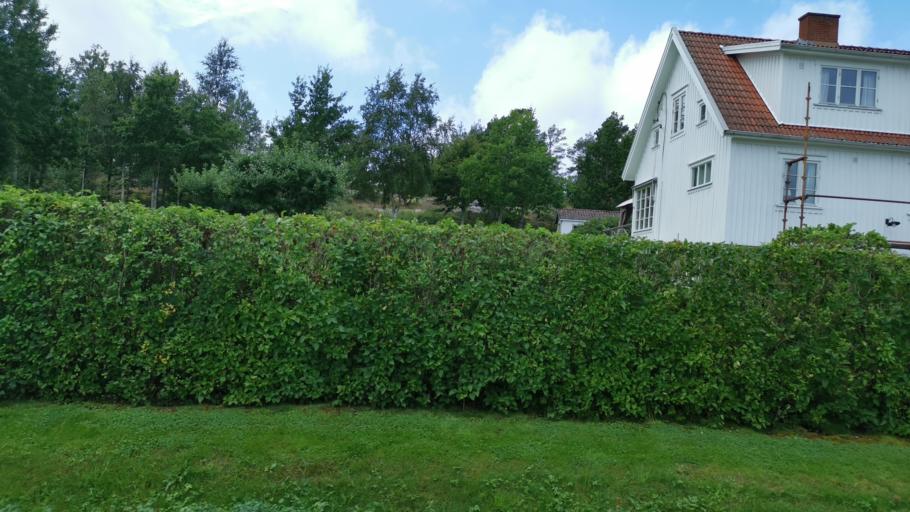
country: SE
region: Vaestra Goetaland
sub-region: Sotenas Kommun
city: Hunnebostrand
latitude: 58.5273
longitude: 11.2960
